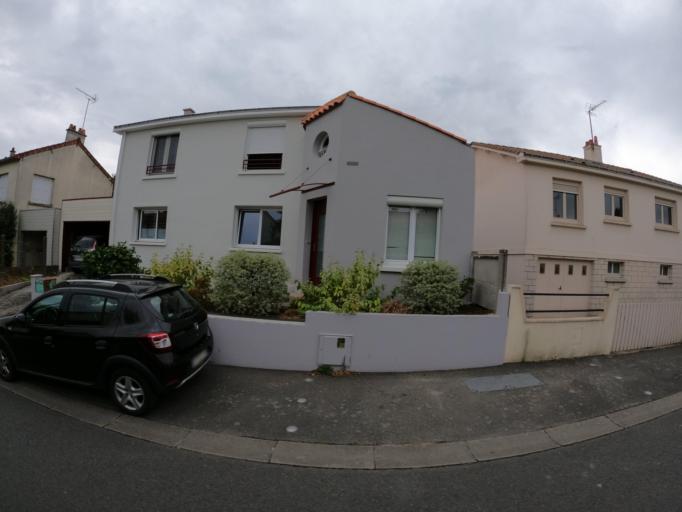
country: FR
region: Pays de la Loire
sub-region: Departement de la Vendee
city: Montaigu
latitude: 46.9761
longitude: -1.3069
